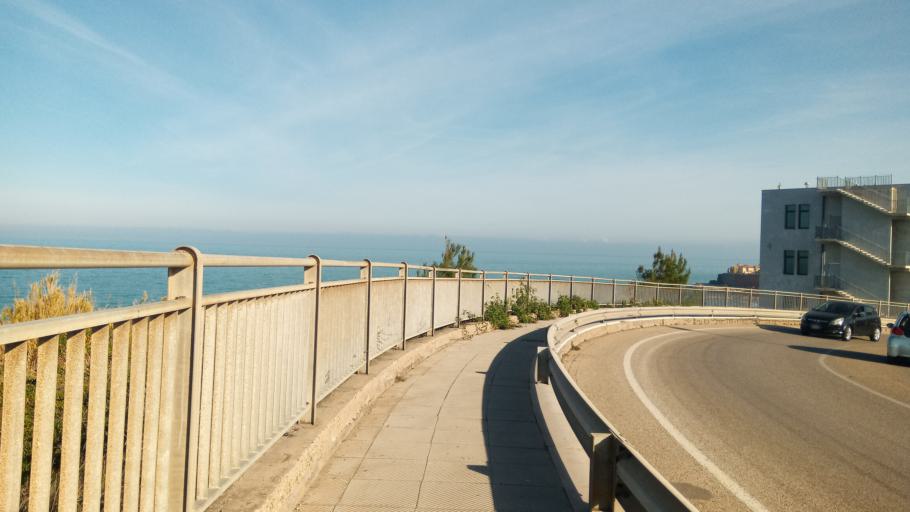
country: IT
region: Molise
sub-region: Provincia di Campobasso
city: Termoli
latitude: 42.0042
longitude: 14.9887
